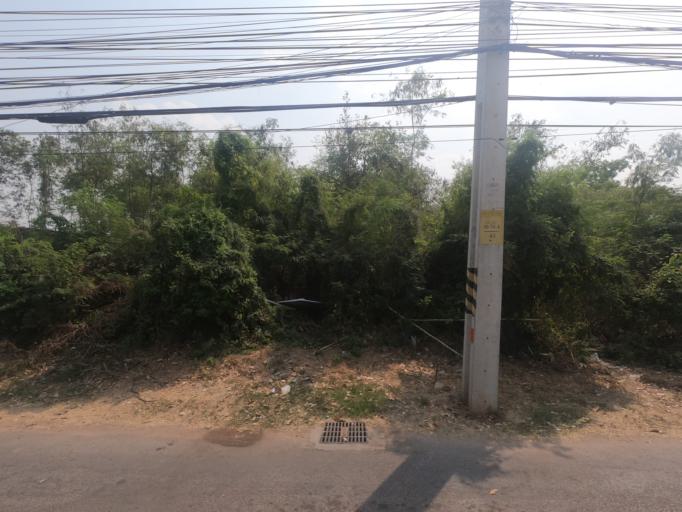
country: TH
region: Nakhon Ratchasima
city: Nakhon Ratchasima
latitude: 14.9570
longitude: 102.0388
